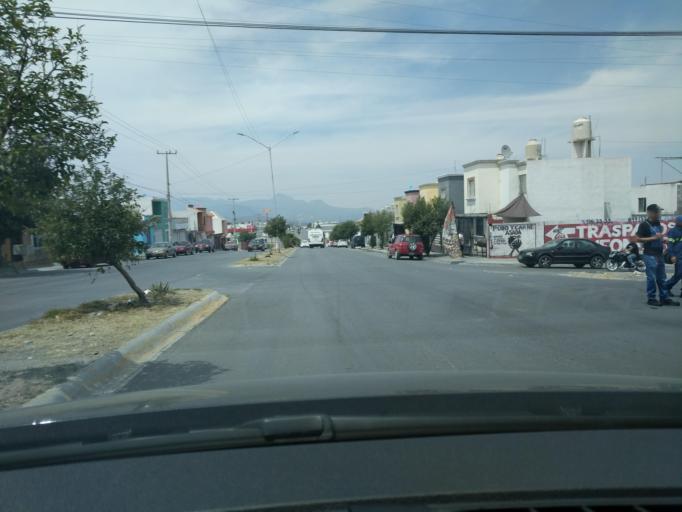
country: MX
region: Coahuila
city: Saltillo
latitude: 25.3522
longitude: -101.0132
